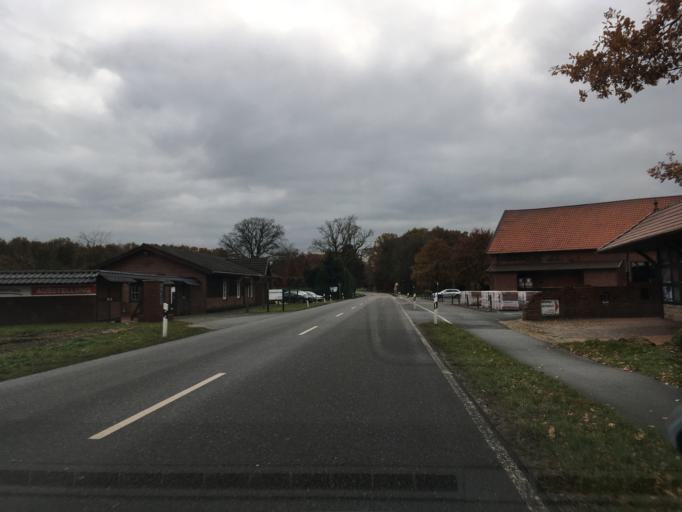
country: DE
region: North Rhine-Westphalia
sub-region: Regierungsbezirk Munster
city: Gescher
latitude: 51.9712
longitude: 7.0143
